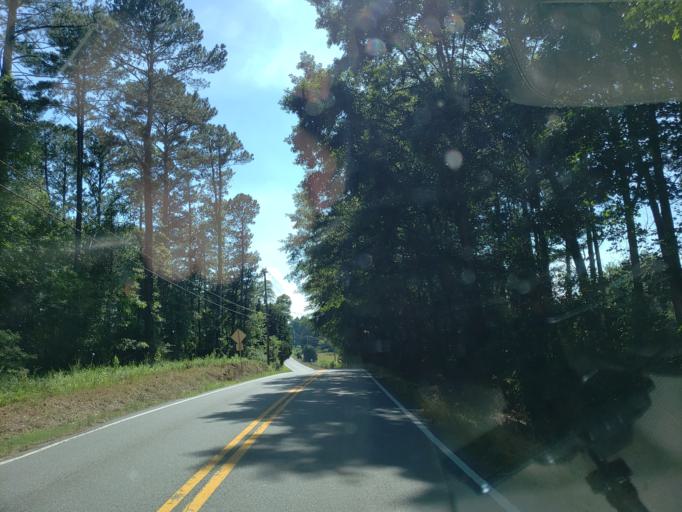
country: US
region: Georgia
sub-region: Cherokee County
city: Woodstock
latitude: 34.1109
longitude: -84.4295
